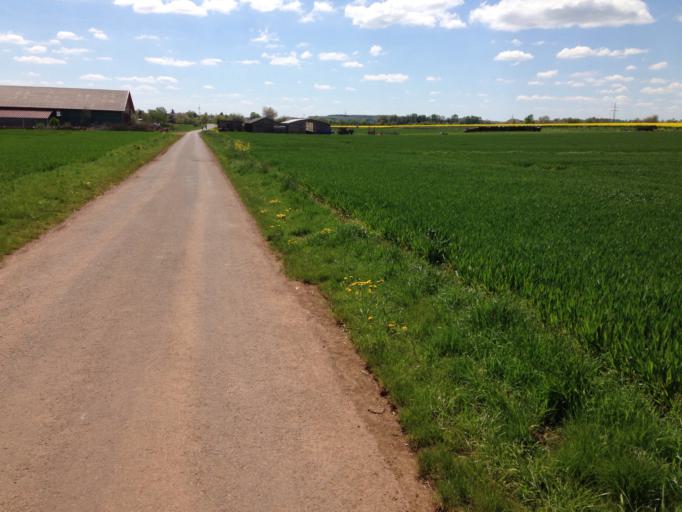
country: DE
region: Hesse
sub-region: Regierungsbezirk Giessen
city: Lich
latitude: 50.5033
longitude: 8.8520
